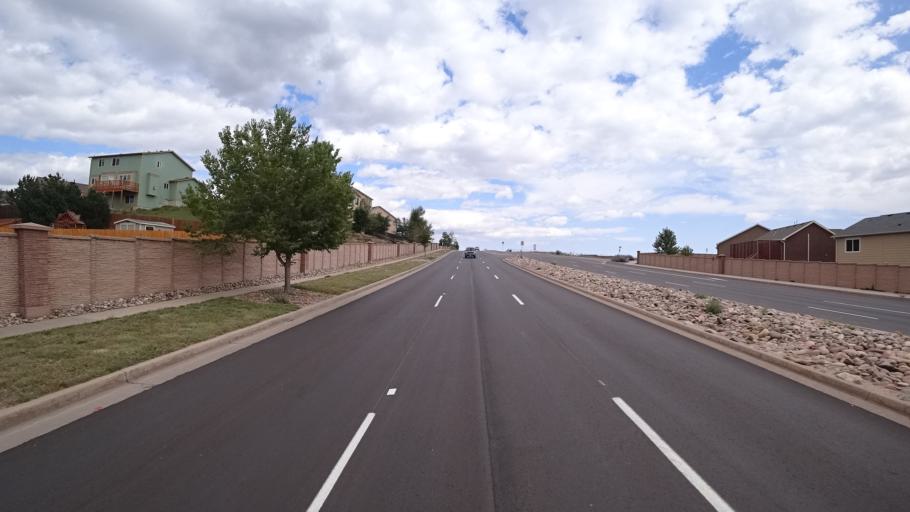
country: US
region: Colorado
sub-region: El Paso County
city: Cimarron Hills
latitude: 38.8867
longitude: -104.6903
